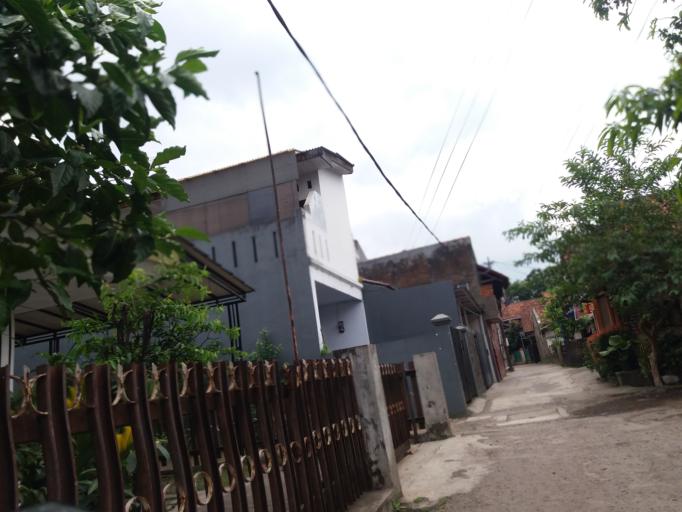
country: ID
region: West Java
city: Bandung
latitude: -6.9213
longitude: 107.6536
